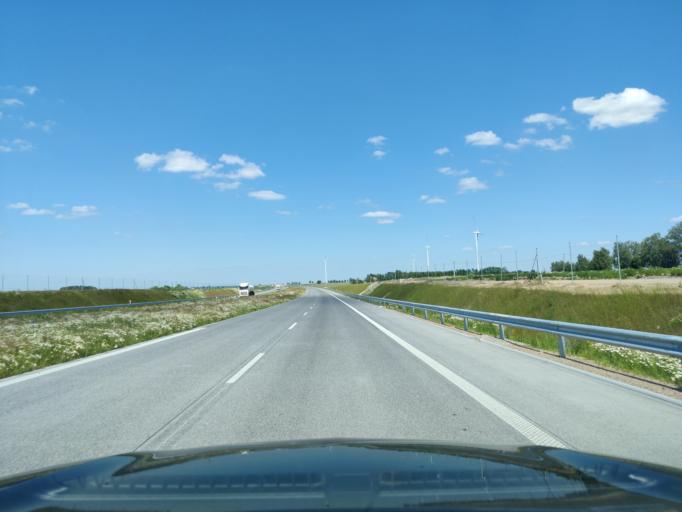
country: PL
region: Masovian Voivodeship
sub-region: Powiat mlawski
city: Wisniewo
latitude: 53.0372
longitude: 20.3552
